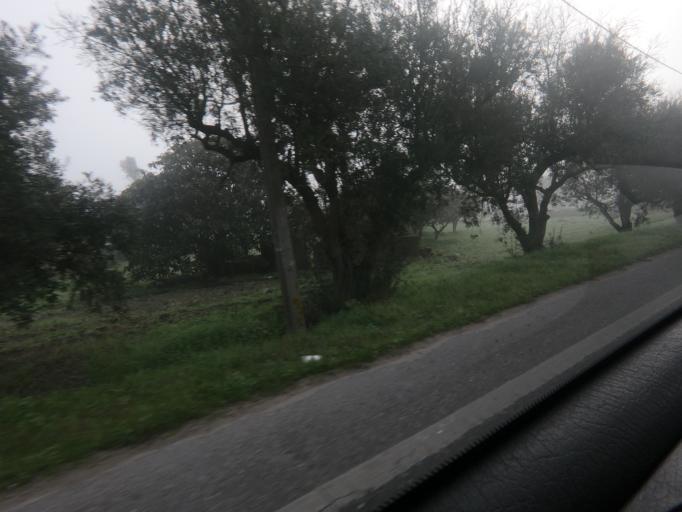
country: PT
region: Setubal
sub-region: Palmela
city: Pinhal Novo
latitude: 38.6153
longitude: -8.9126
